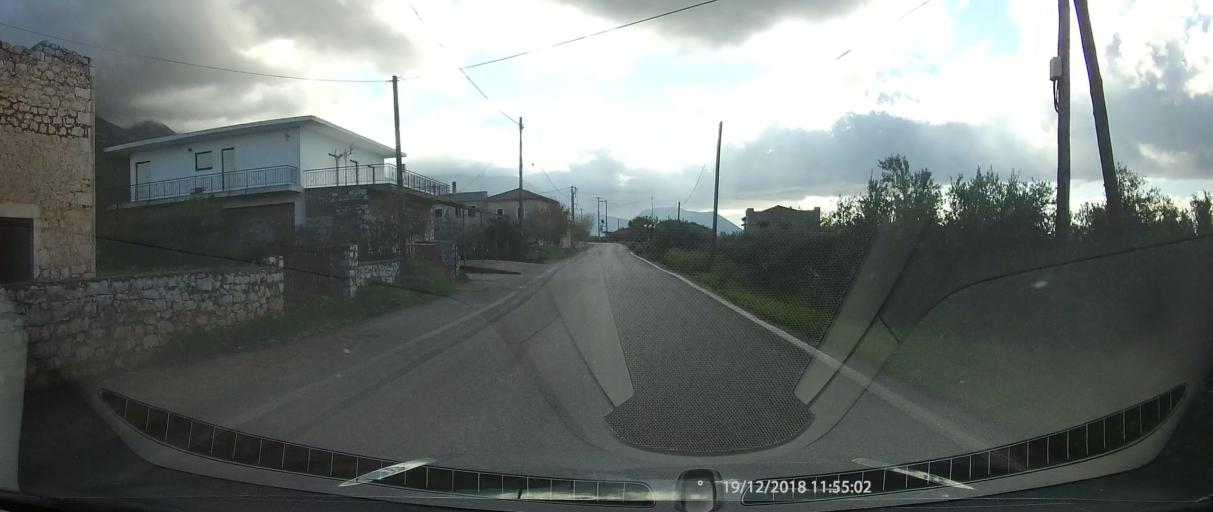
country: GR
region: Peloponnese
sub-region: Nomos Lakonias
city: Gytheio
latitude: 36.6118
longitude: 22.3918
